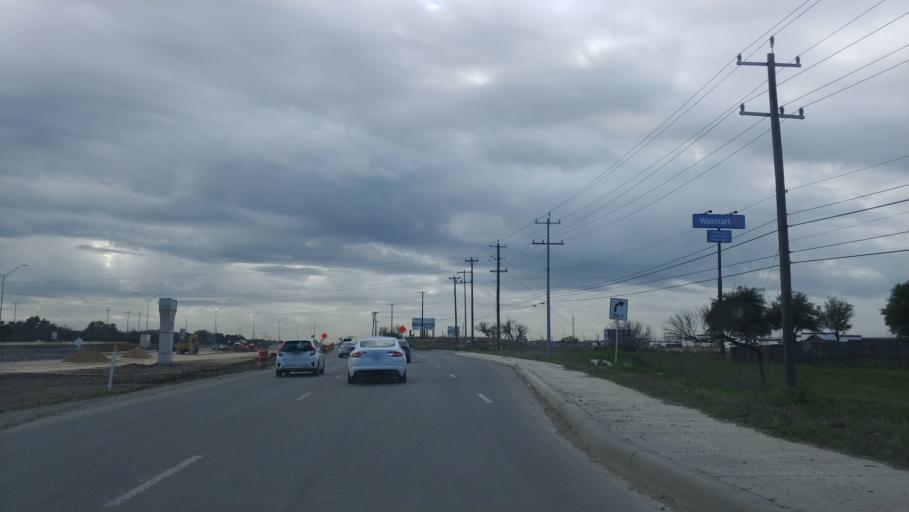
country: US
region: Texas
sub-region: Bexar County
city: Lackland Air Force Base
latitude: 29.4337
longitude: -98.7120
